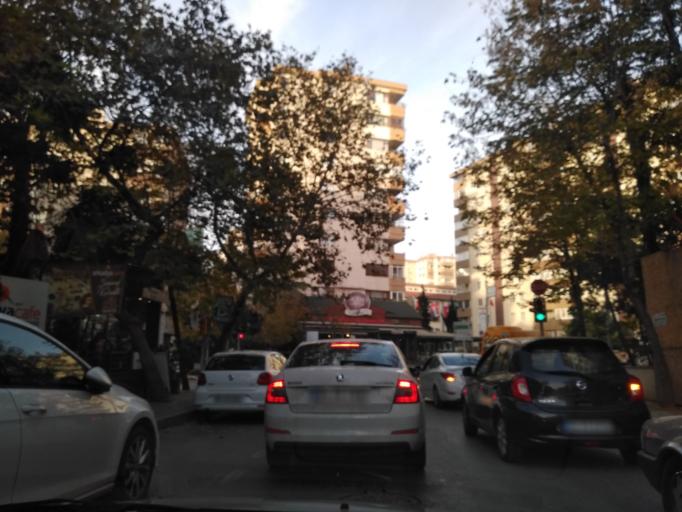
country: TR
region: Istanbul
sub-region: Atasehir
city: Atasehir
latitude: 40.9783
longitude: 29.0916
